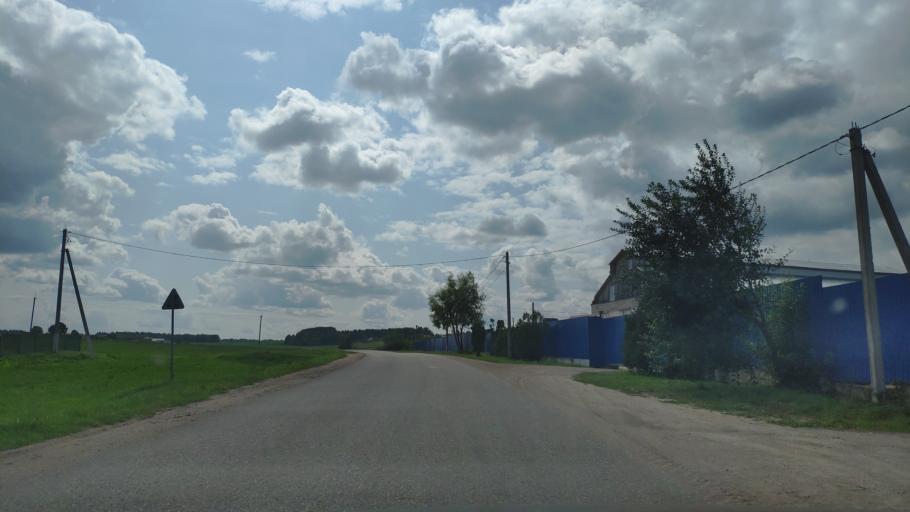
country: BY
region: Minsk
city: Khatsyezhyna
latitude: 53.8632
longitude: 27.3137
